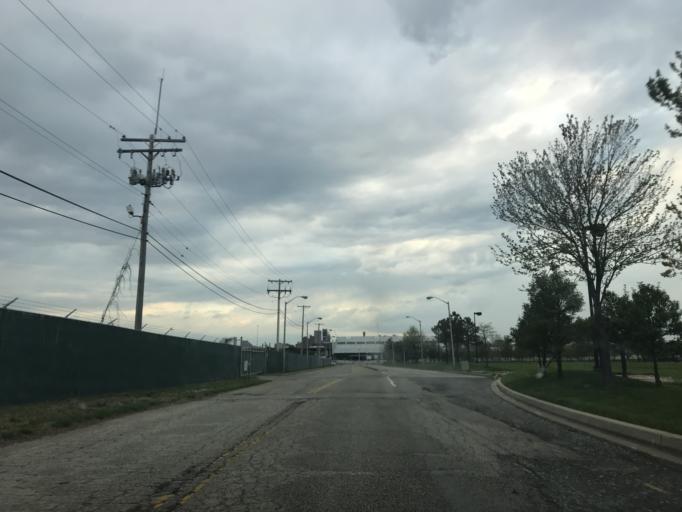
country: US
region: Maryland
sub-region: City of Baltimore
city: Baltimore
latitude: 39.2596
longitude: -76.6105
